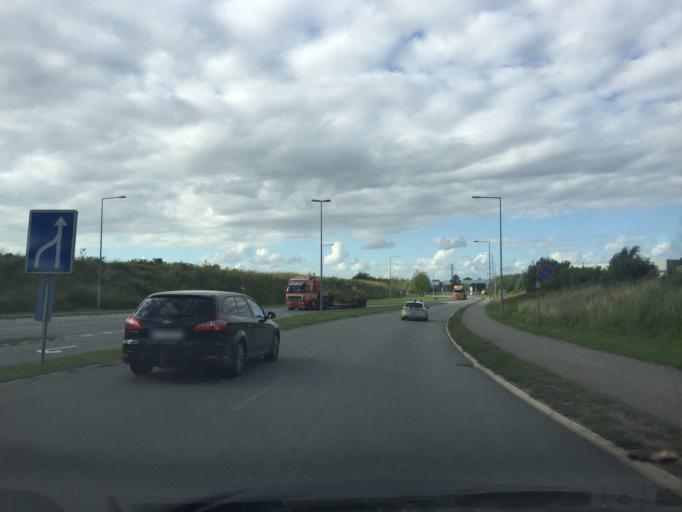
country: DK
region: Capital Region
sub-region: Vallensbaek Kommune
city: Vallensbaek
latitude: 55.6442
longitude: 12.3721
